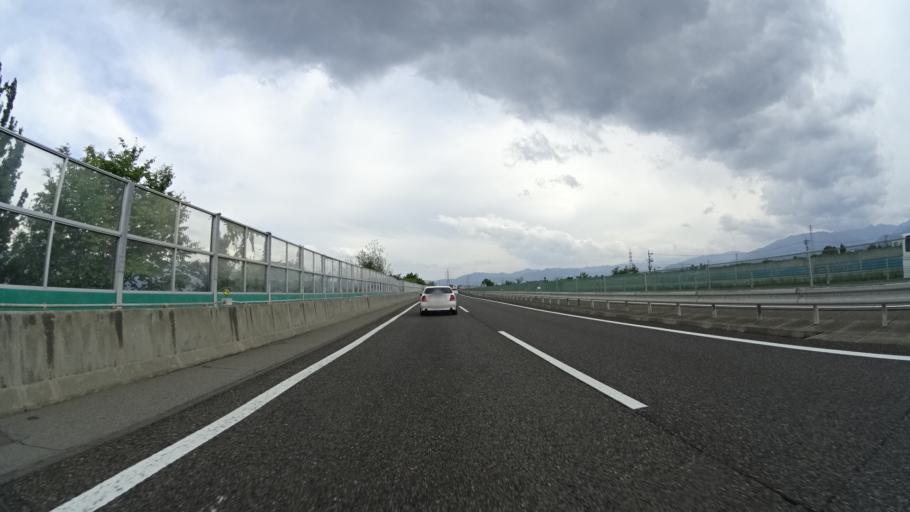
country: JP
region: Nagano
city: Matsumoto
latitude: 36.1984
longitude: 137.9349
